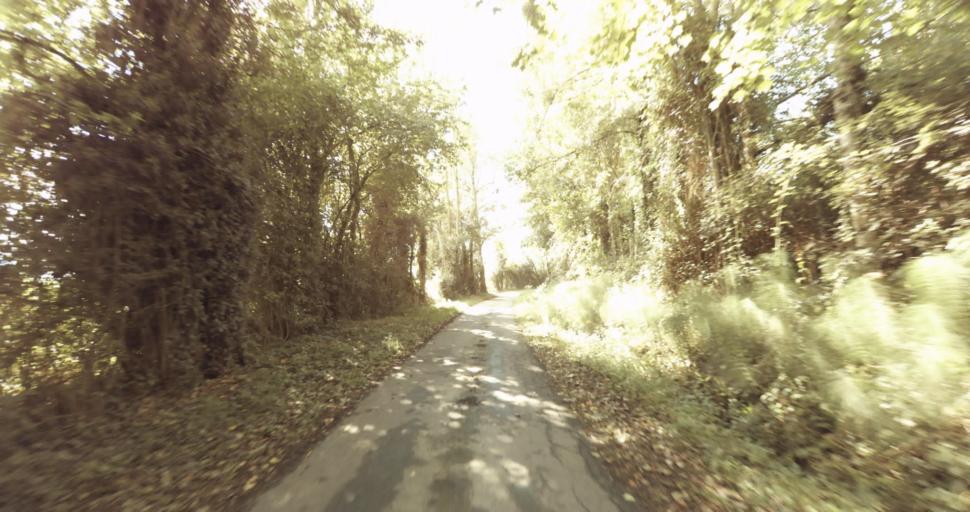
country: FR
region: Lower Normandy
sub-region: Departement de l'Orne
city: Gace
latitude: 48.8118
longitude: 0.2155
